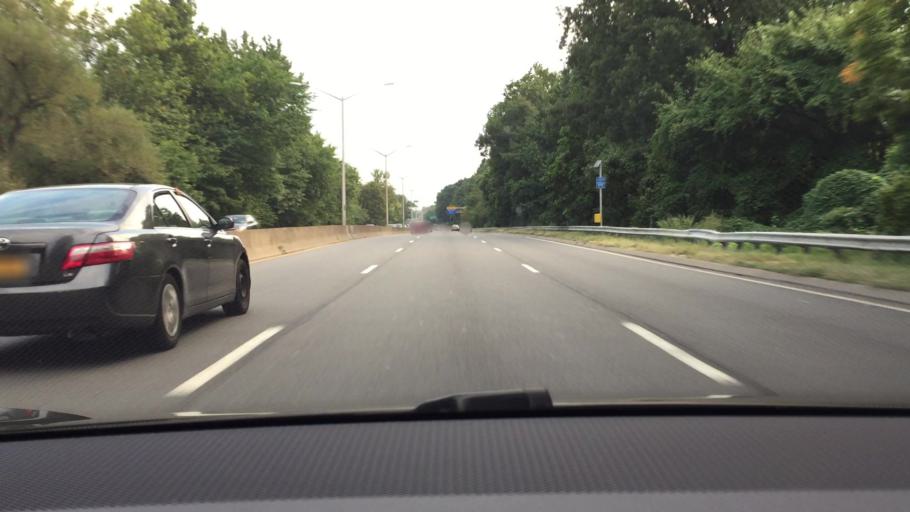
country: US
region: New York
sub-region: Bronx
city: Eastchester
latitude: 40.8890
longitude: -73.8660
